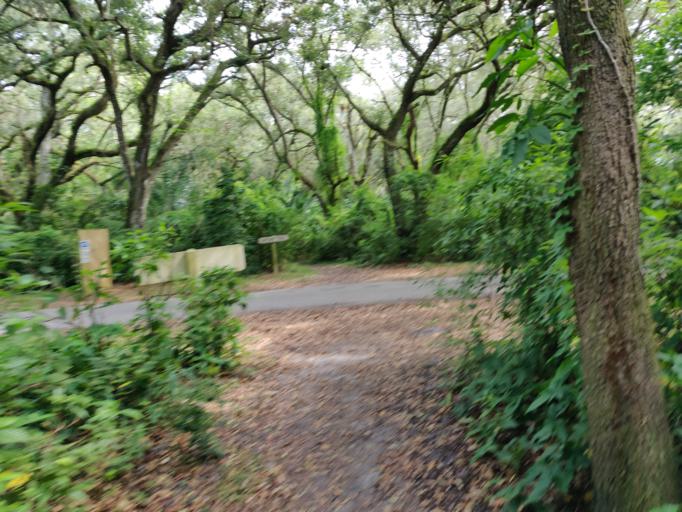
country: US
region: Florida
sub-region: Broward County
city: Cooper City
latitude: 26.0747
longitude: -80.2762
